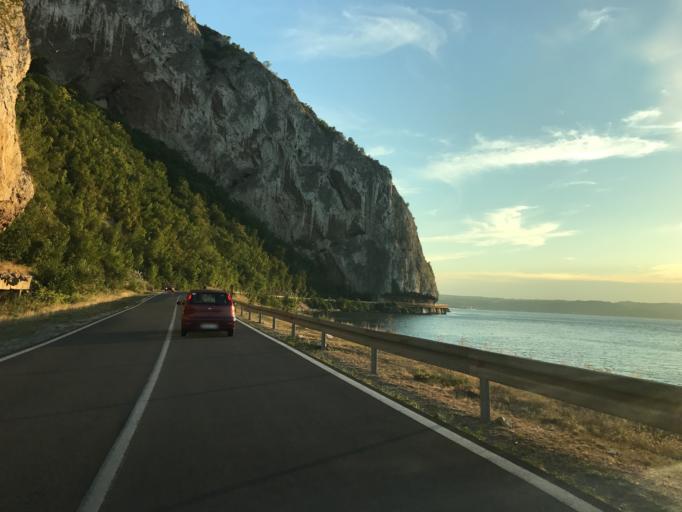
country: RO
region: Caras-Severin
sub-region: Comuna Pescari
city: Coronini
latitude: 44.6600
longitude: 21.6702
